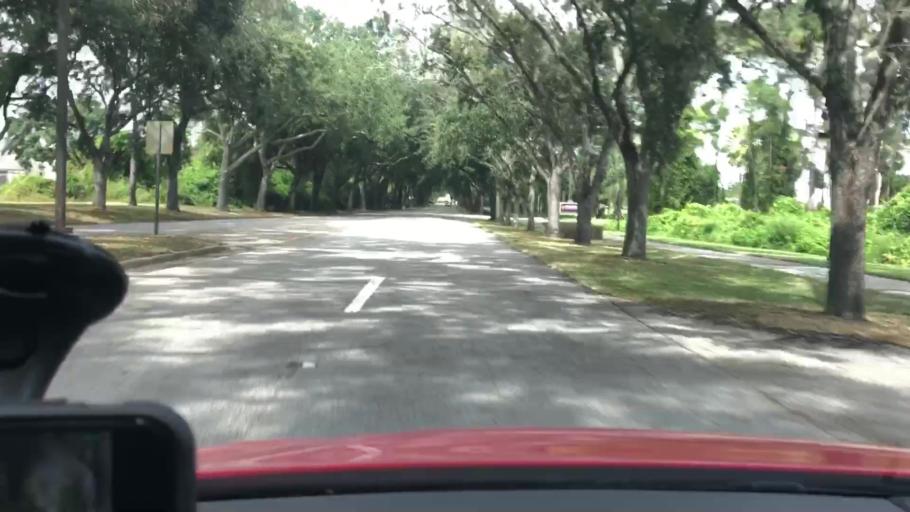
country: US
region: Florida
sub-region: Volusia County
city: Port Orange
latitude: 29.1219
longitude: -81.0182
